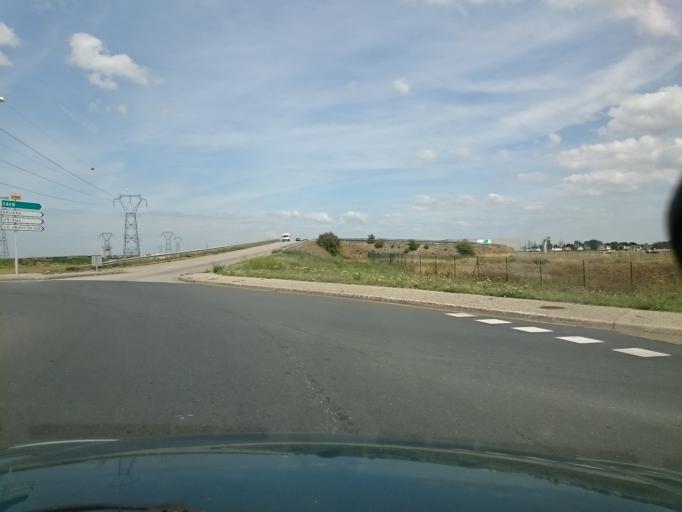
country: FR
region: Lower Normandy
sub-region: Departement du Calvados
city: Ifs
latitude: 49.1361
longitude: -0.3367
